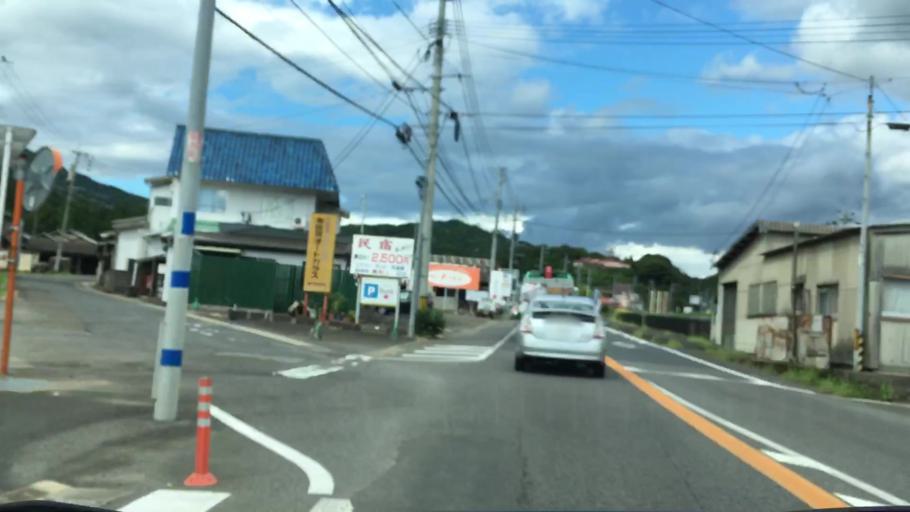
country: JP
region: Saga Prefecture
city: Imaricho-ko
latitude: 33.2825
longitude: 129.8974
